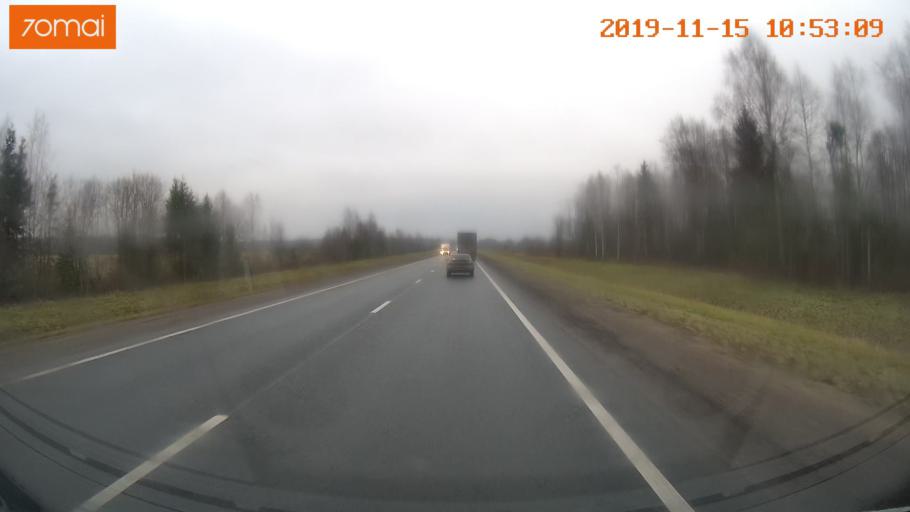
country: RU
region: Vologda
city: Chebsara
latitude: 59.1706
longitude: 38.7483
